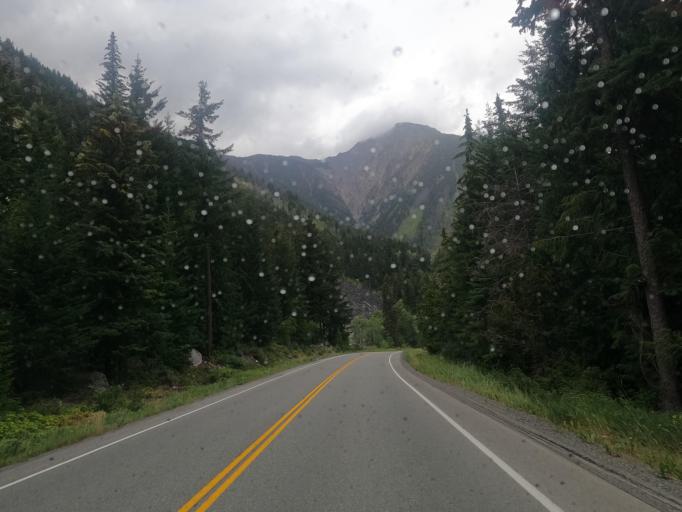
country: CA
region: British Columbia
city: Lillooet
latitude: 50.5262
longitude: -122.1611
